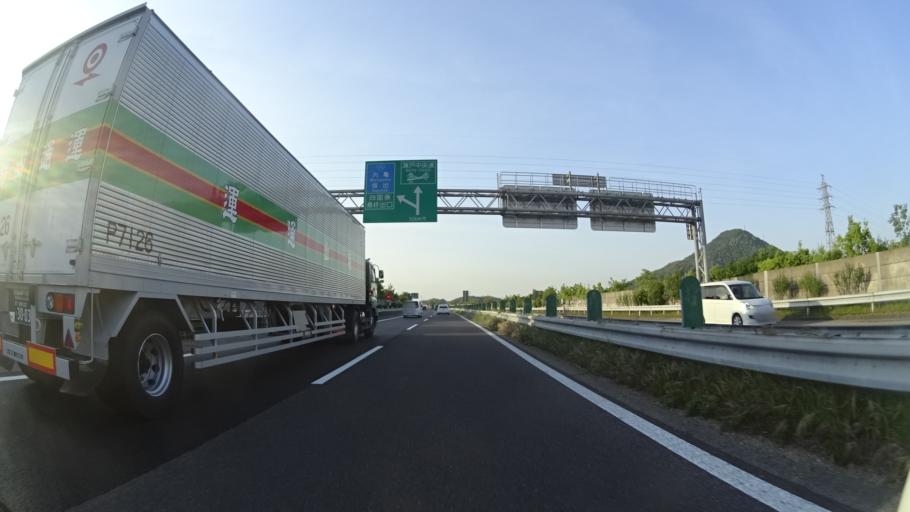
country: JP
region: Kagawa
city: Sakaidecho
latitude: 34.2853
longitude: 133.8516
